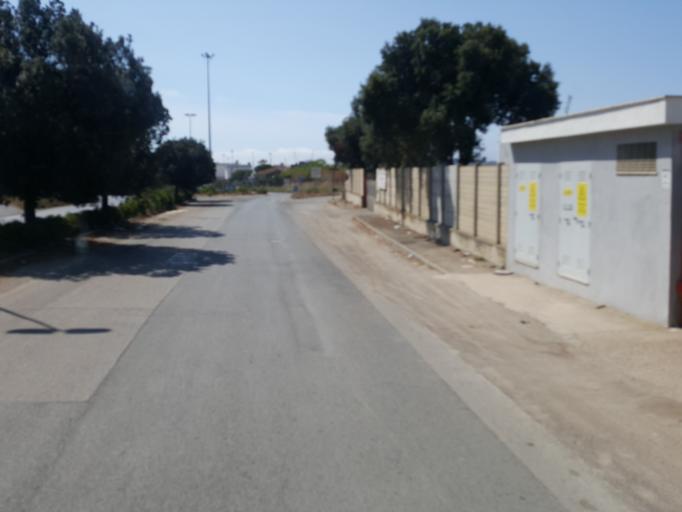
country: IT
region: Latium
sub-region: Citta metropolitana di Roma Capitale
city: Aurelia
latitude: 42.1170
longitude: 11.7787
